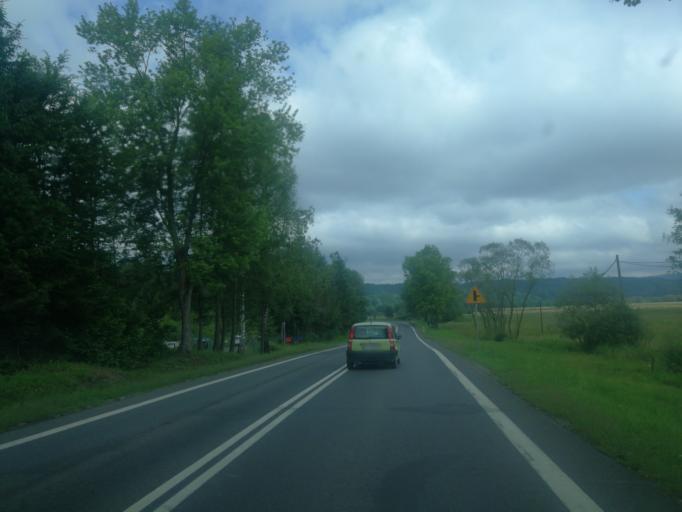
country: PL
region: Subcarpathian Voivodeship
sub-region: Powiat leski
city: Lesko
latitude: 49.4893
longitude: 22.3216
